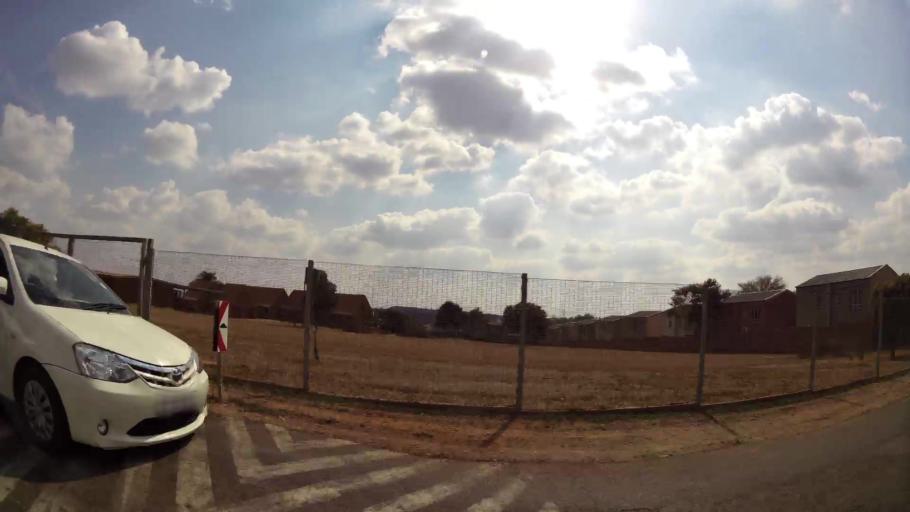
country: ZA
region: Gauteng
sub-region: City of Tshwane Metropolitan Municipality
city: Centurion
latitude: -25.8094
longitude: 28.3480
